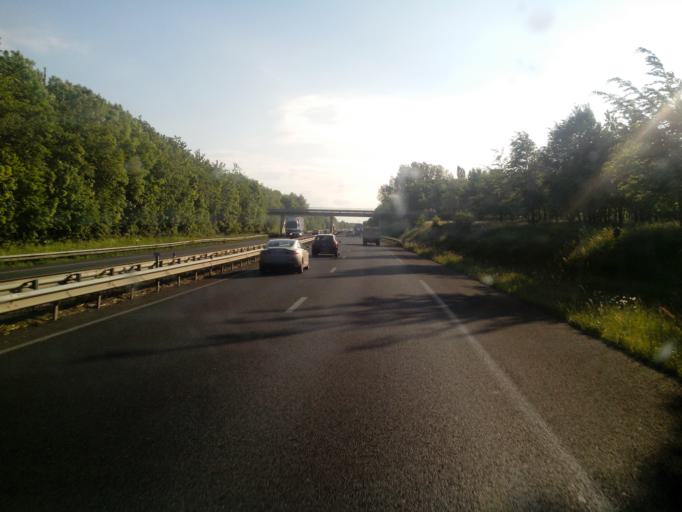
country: FR
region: Lower Normandy
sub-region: Departement du Calvados
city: Grainville-sur-Odon
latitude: 49.1427
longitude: -0.5370
